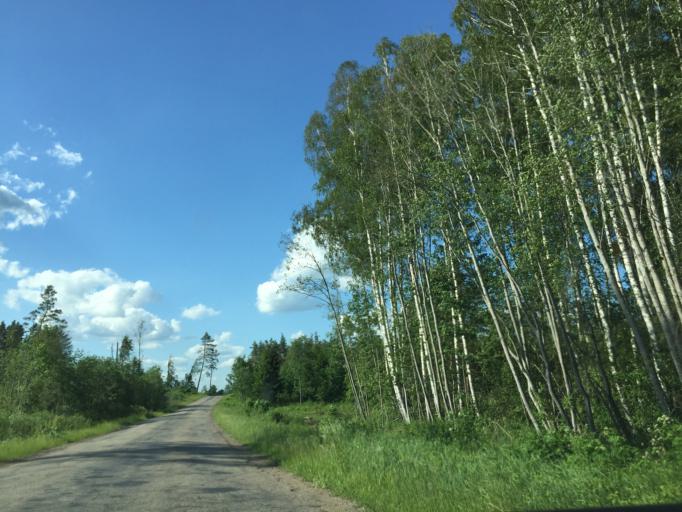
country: LV
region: Jaunpils
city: Jaunpils
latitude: 56.8936
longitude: 22.9783
